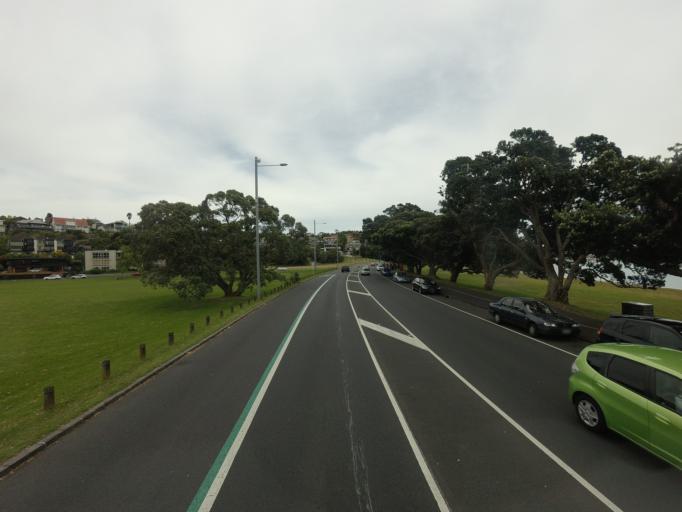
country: NZ
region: Auckland
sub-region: Auckland
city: Auckland
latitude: -36.8514
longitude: 174.8164
